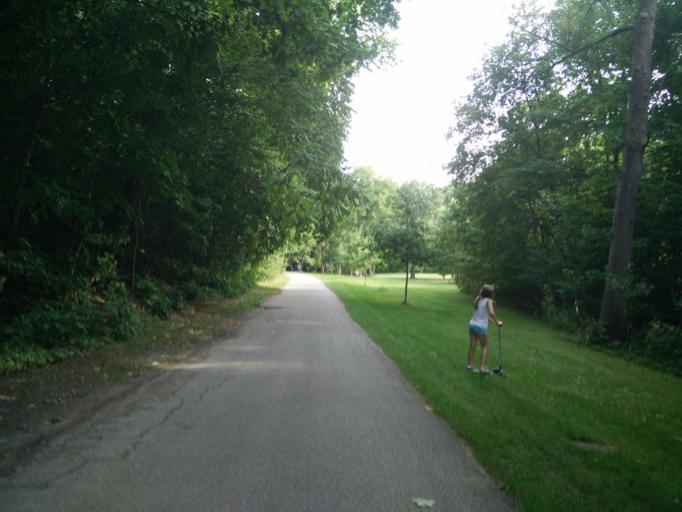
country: CA
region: Ontario
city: Etobicoke
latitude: 43.6538
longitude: -79.5018
